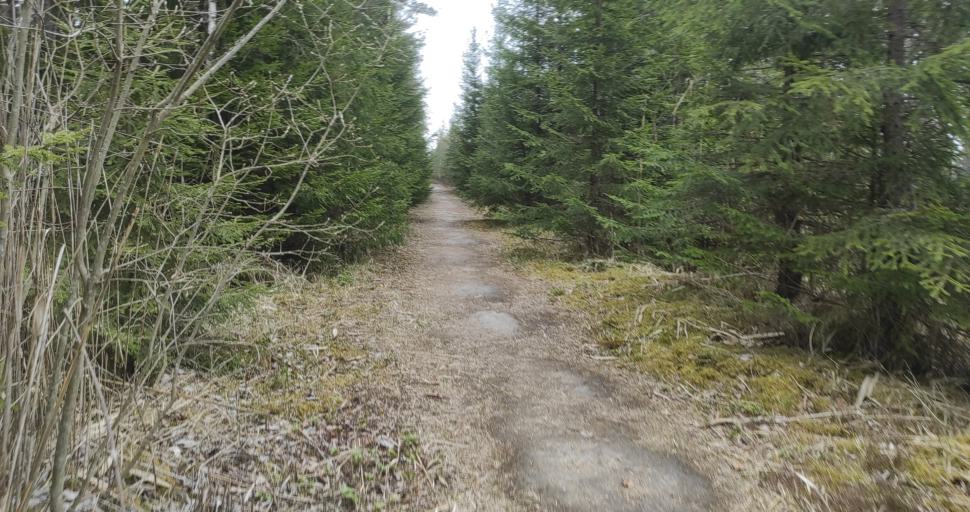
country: LV
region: Dundaga
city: Dundaga
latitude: 57.3454
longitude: 22.1497
